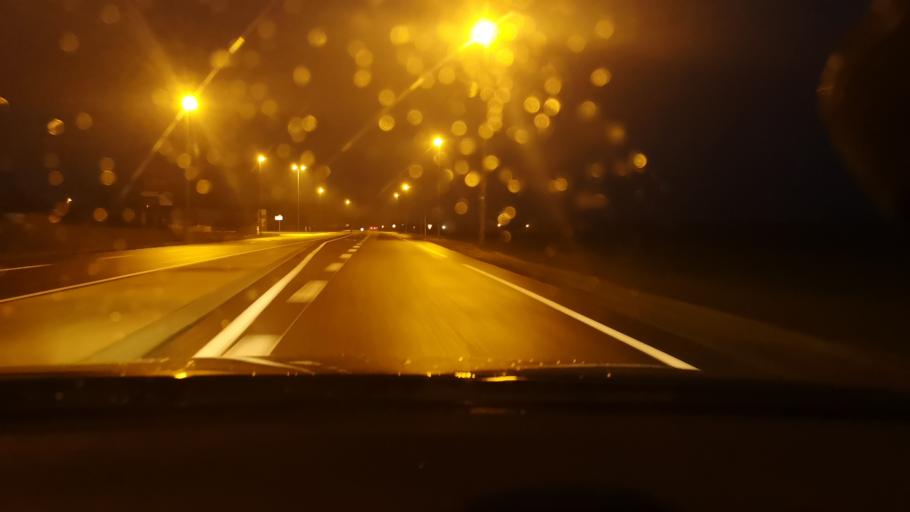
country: FR
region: Bourgogne
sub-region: Departement de Saone-et-Loire
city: Champforgeuil
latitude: 46.8413
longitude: 4.8148
